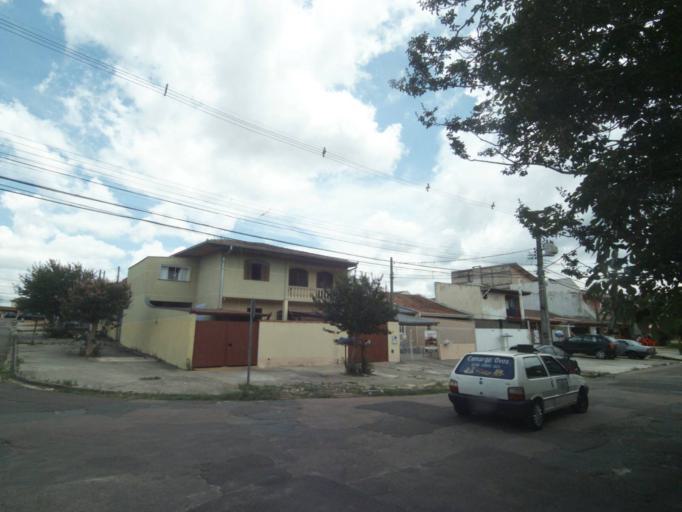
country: BR
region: Parana
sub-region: Curitiba
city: Curitiba
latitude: -25.4720
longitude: -49.3395
